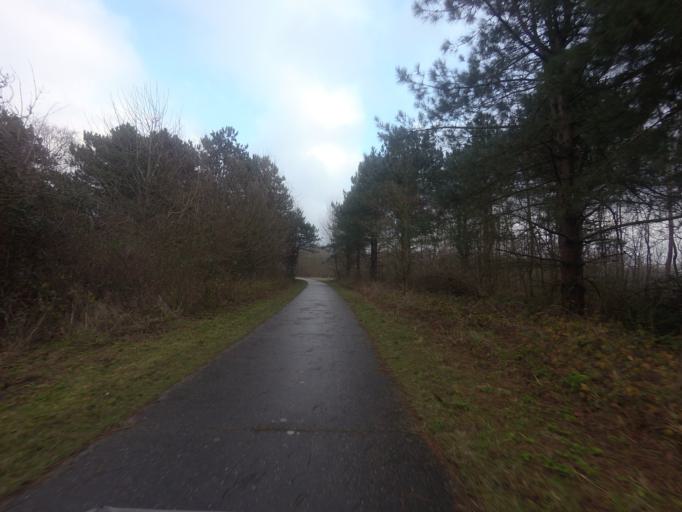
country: NL
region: North Holland
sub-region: Gemeente Texel
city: Den Burg
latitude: 53.1646
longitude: 4.8491
